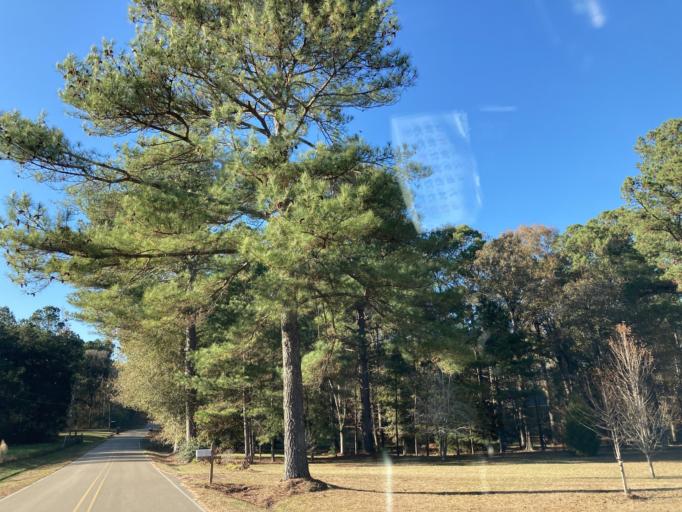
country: US
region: Mississippi
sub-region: Lamar County
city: Sumrall
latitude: 31.3996
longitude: -89.5768
